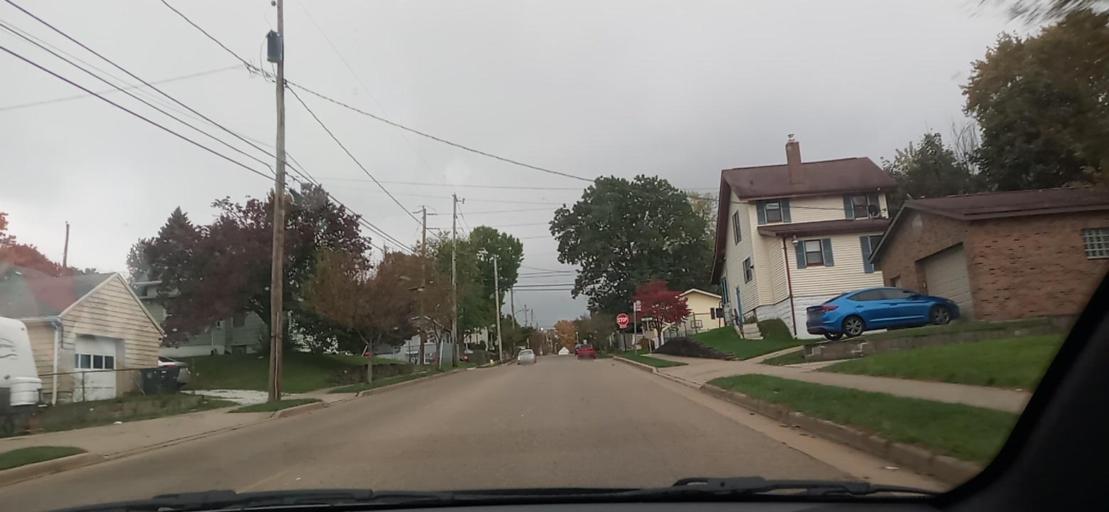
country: US
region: Ohio
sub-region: Summit County
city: Portage Lakes
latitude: 41.0466
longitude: -81.5634
